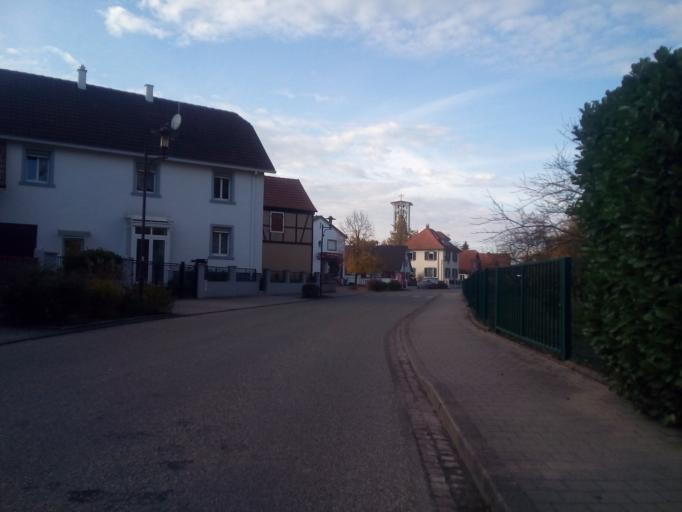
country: FR
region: Alsace
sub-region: Departement du Bas-Rhin
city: Herrlisheim
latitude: 48.7100
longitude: 7.9154
